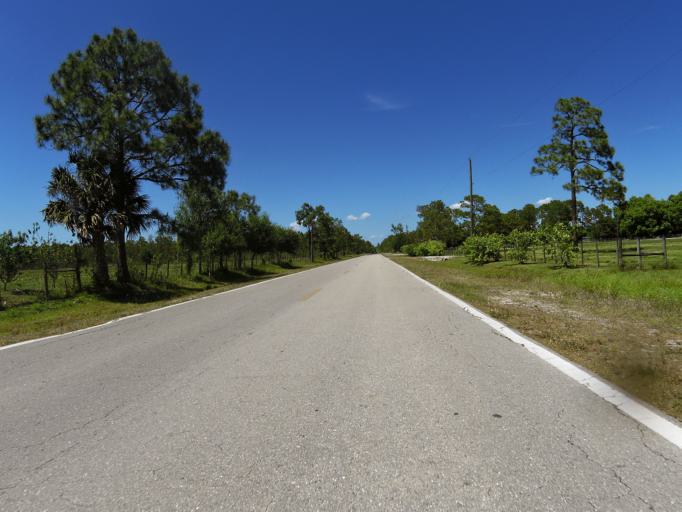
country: US
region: Florida
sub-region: Collier County
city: Orangetree
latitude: 26.3694
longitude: -81.5877
